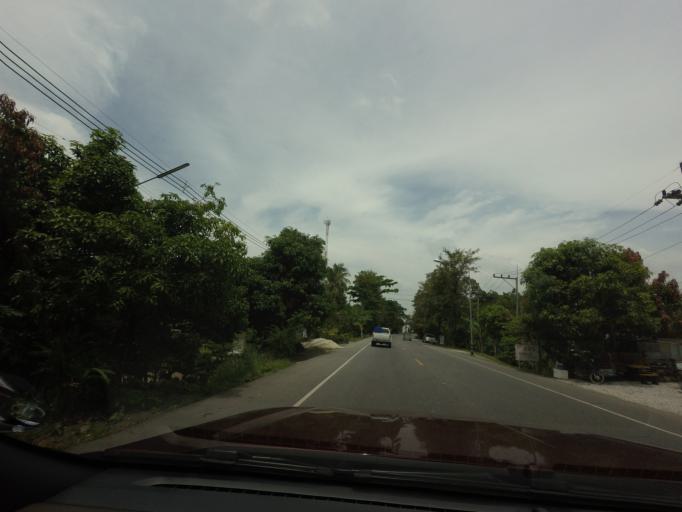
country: TH
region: Yala
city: Yala
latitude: 6.6118
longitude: 101.3063
